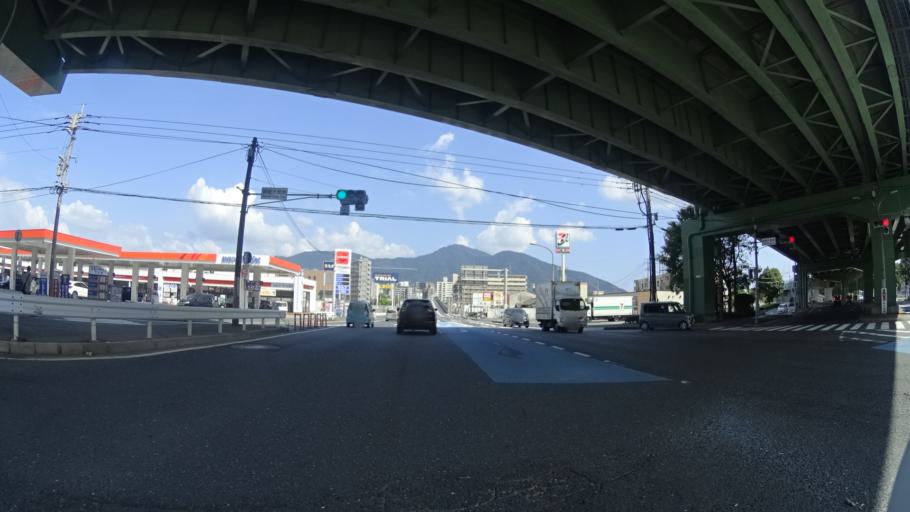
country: JP
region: Fukuoka
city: Kitakyushu
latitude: 33.8652
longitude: 130.8724
